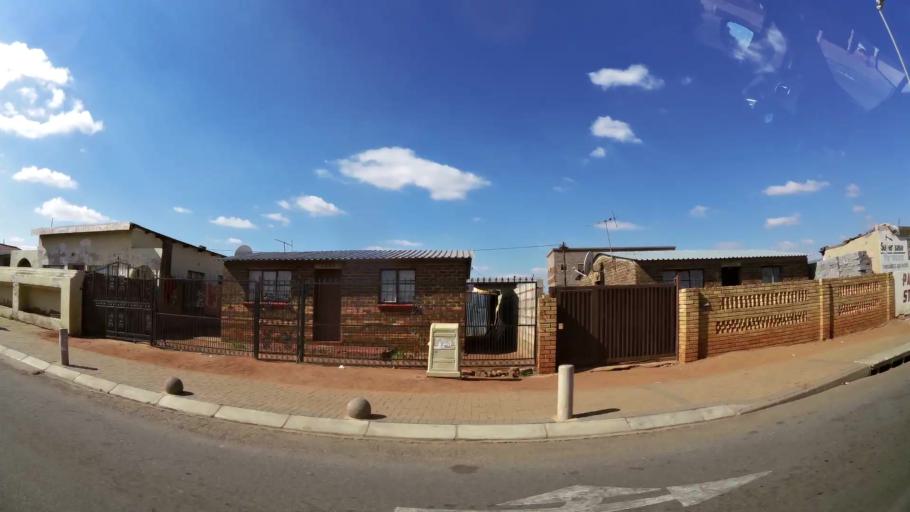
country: ZA
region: Gauteng
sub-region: West Rand District Municipality
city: Krugersdorp
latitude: -26.1611
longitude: 27.7815
